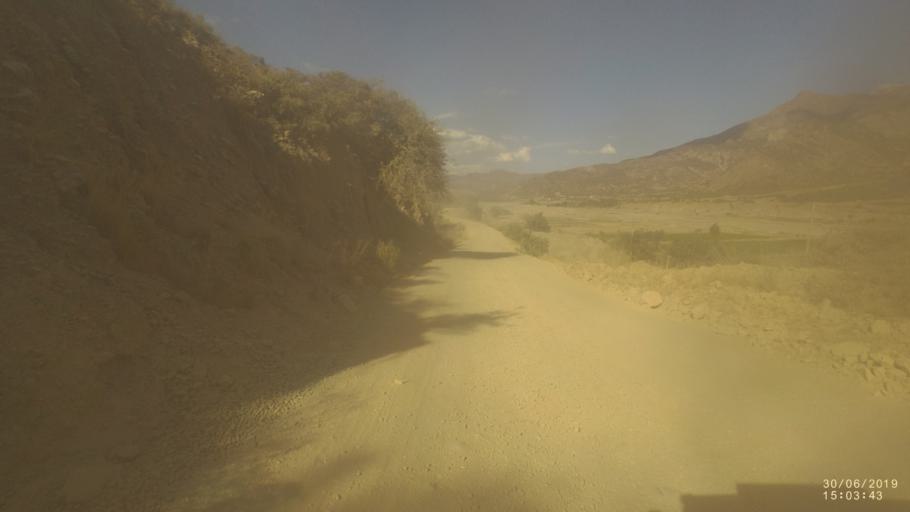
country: BO
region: Cochabamba
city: Irpa Irpa
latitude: -17.7315
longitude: -66.3253
